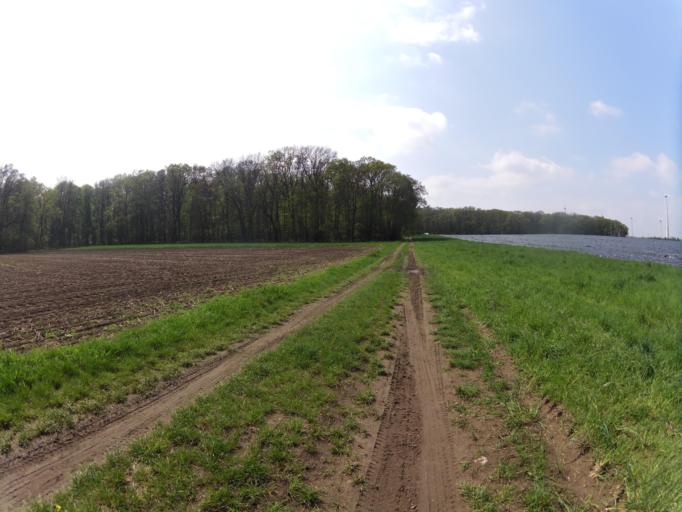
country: DE
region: Bavaria
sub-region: Regierungsbezirk Unterfranken
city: Sommerhausen
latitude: 49.7070
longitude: 10.0646
